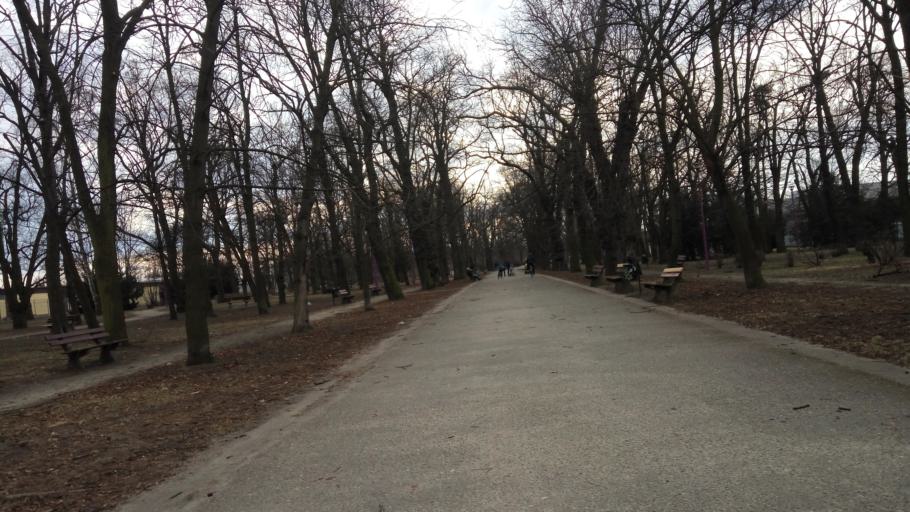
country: PL
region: Lower Silesian Voivodeship
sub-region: Powiat wroclawski
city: Wroclaw
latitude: 51.0881
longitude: 17.0303
